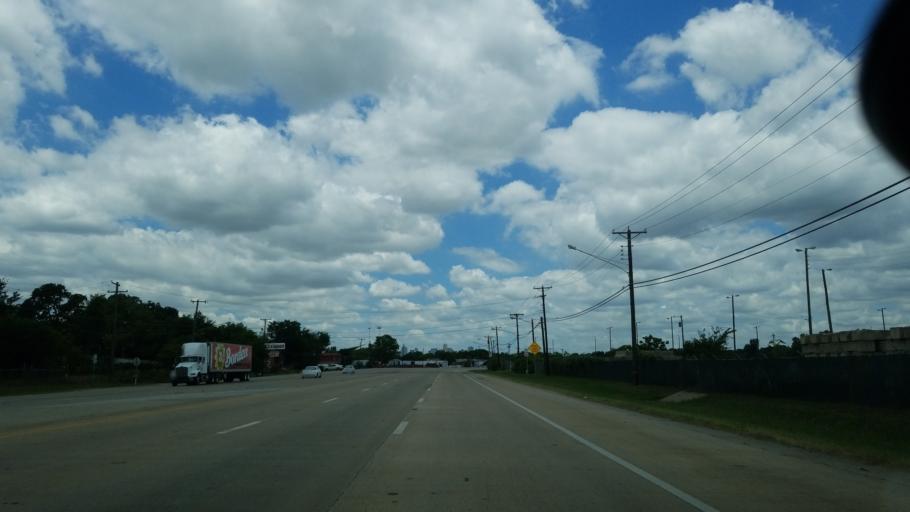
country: US
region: Texas
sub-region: Dallas County
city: Hutchins
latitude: 32.7179
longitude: -96.7566
